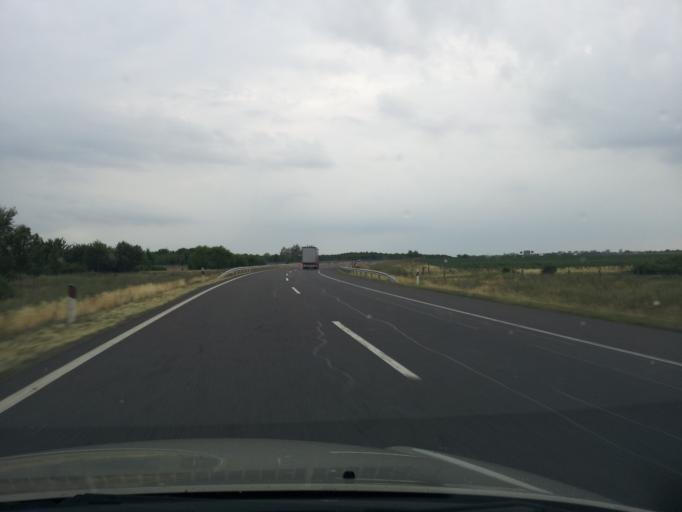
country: HU
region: Borsod-Abauj-Zemplen
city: Emod
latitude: 47.8824
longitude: 20.8317
